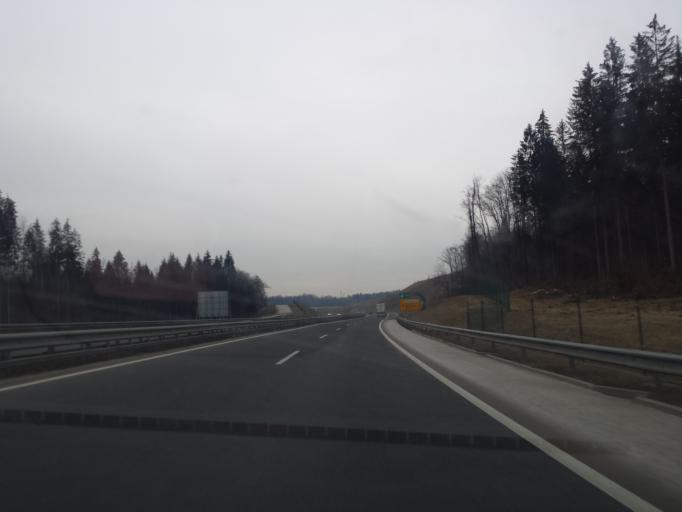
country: SI
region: Trebnje
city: Trebnje
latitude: 45.8931
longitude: 15.0588
